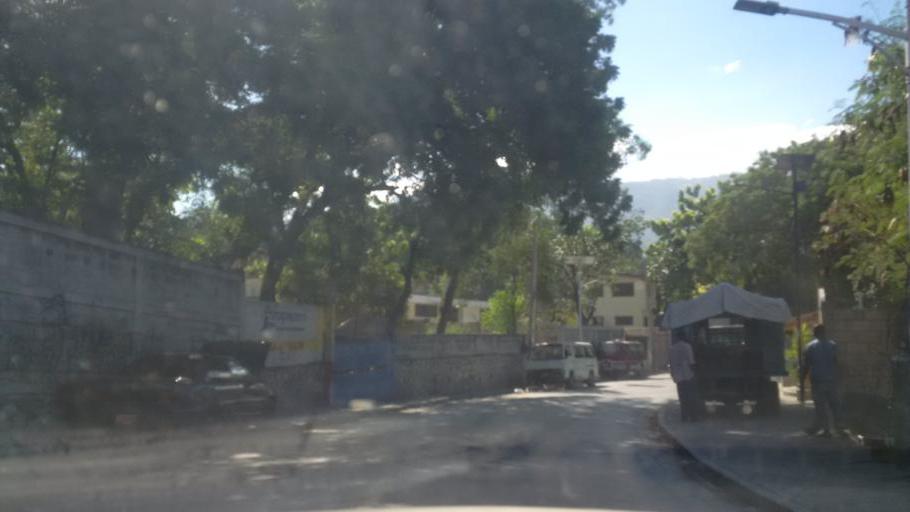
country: HT
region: Ouest
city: Port-au-Prince
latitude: 18.5461
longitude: -72.3209
